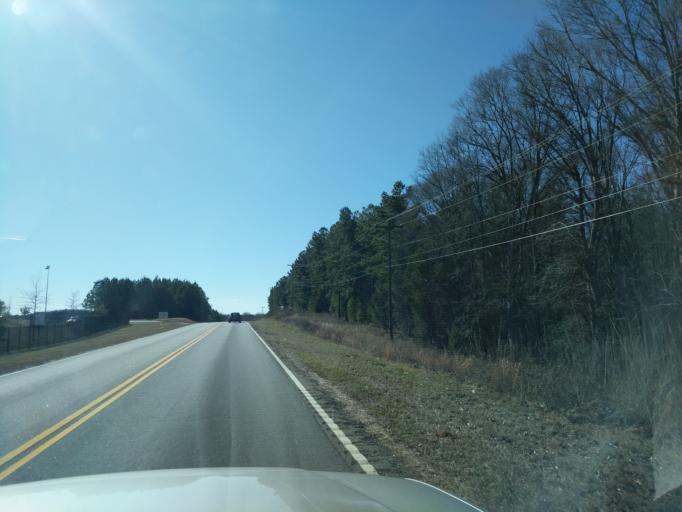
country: US
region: South Carolina
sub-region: Anderson County
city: Homeland Park
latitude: 34.4612
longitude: -82.6889
